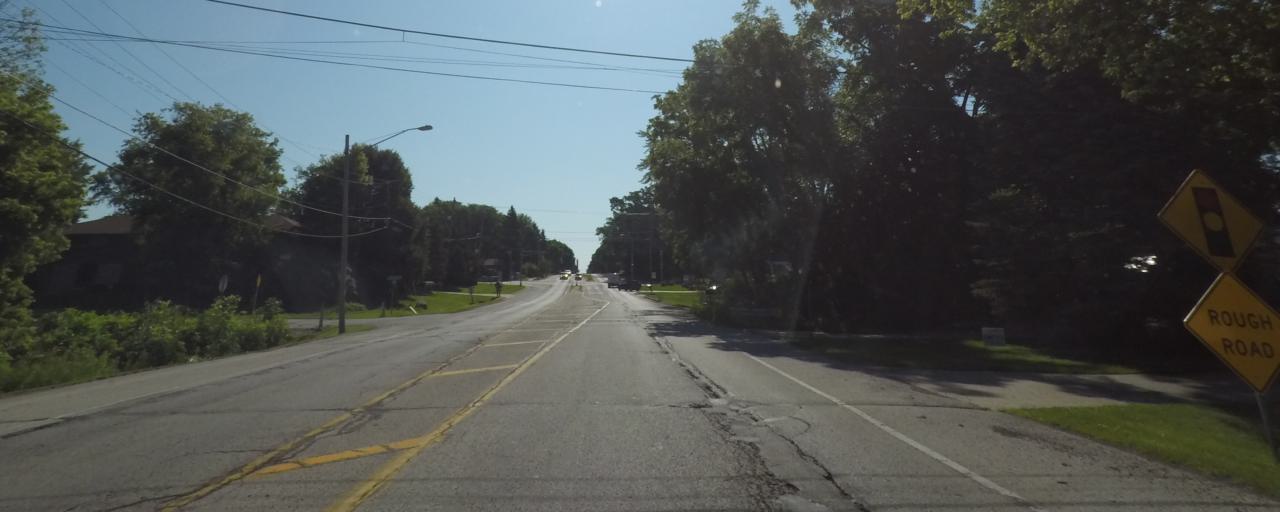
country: US
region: Wisconsin
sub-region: Waukesha County
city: New Berlin
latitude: 42.9955
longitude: -88.0699
